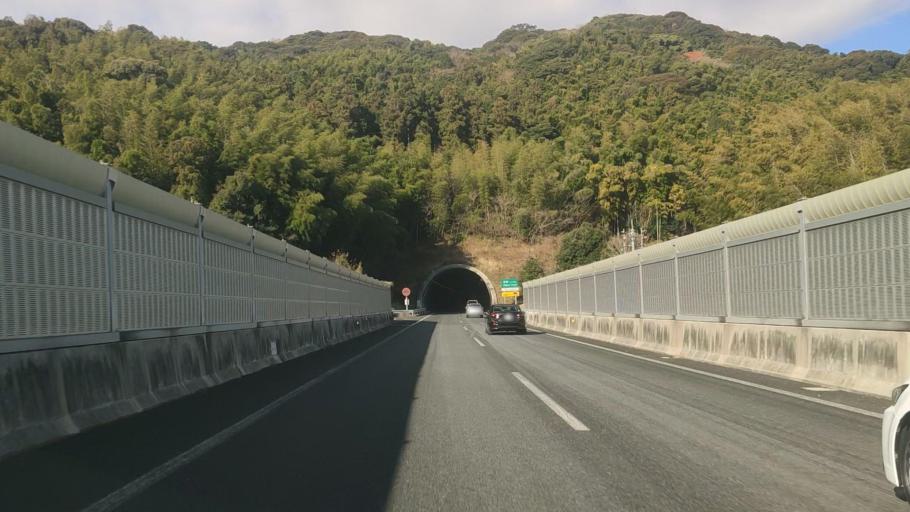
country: JP
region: Fukuoka
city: Kanda
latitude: 33.8057
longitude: 130.9218
